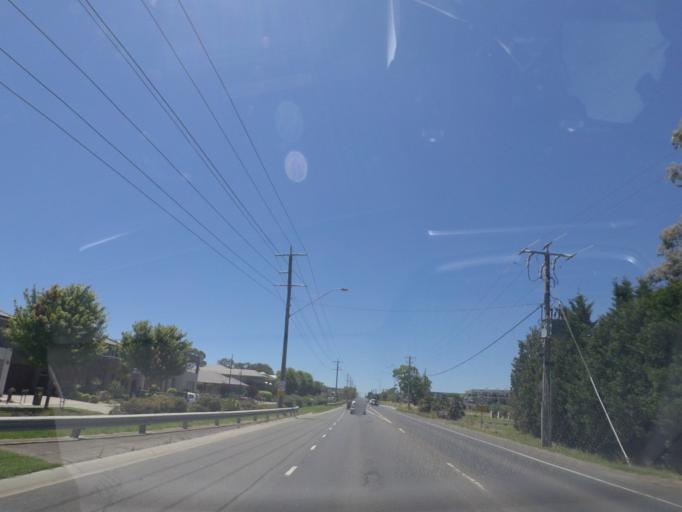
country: AU
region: Victoria
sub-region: Whittlesea
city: Epping
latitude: -37.6324
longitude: 145.0272
